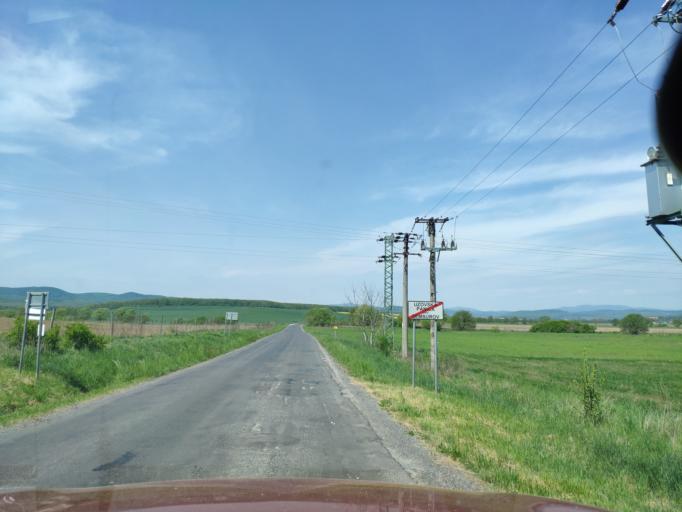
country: SK
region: Banskobystricky
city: Rimavska Sobota
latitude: 48.4157
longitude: 20.1288
